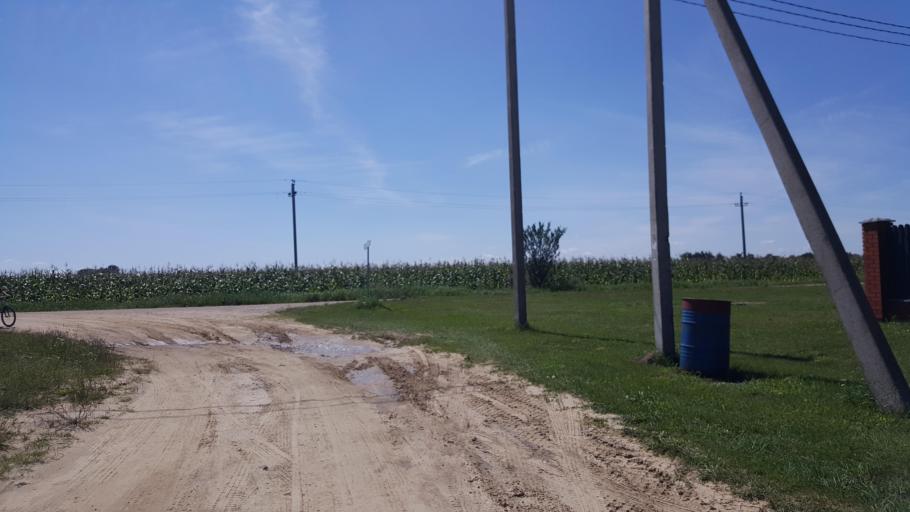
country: BY
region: Brest
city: Charnawchytsy
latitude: 52.2107
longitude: 23.7298
